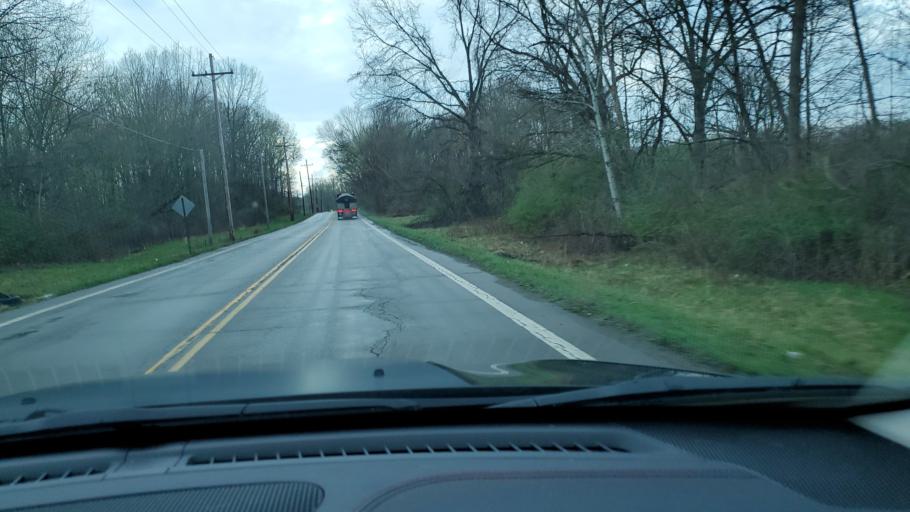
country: US
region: Ohio
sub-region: Trumbull County
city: Niles
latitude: 41.1682
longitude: -80.7555
